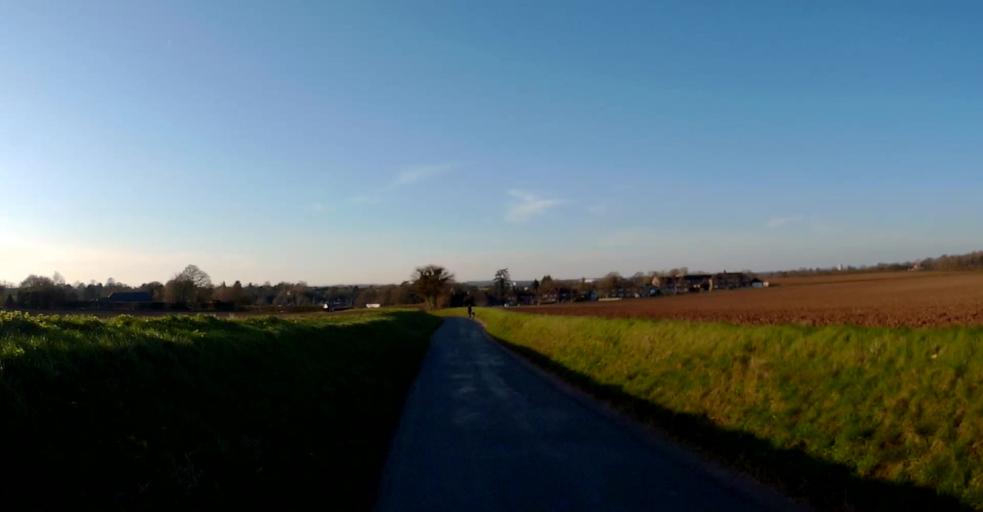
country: GB
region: England
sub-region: Hampshire
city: Basingstoke
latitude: 51.2345
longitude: -1.0923
